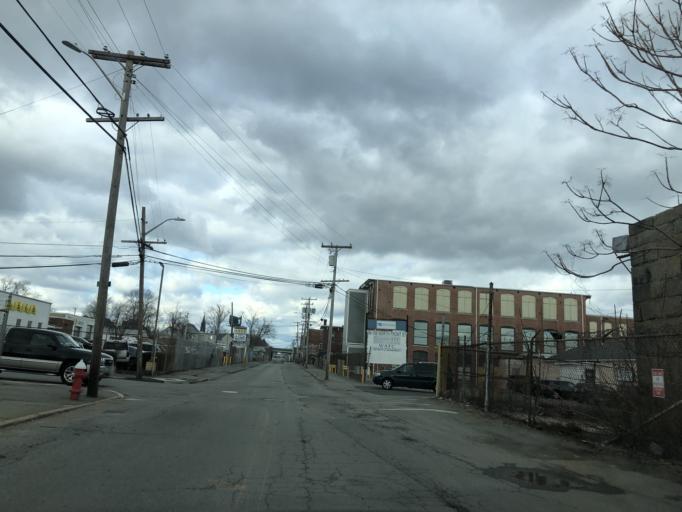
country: US
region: Massachusetts
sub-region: Bristol County
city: New Bedford
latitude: 41.6516
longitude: -70.9244
